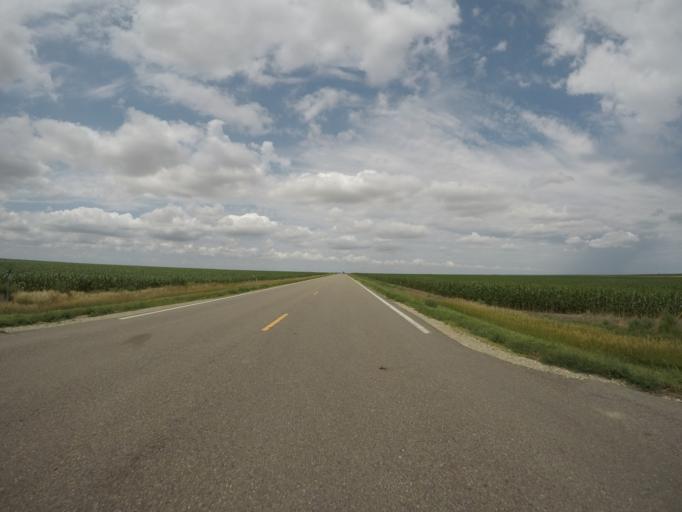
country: US
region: Kansas
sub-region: Rawlins County
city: Atwood
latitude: 39.6695
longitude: -101.0566
